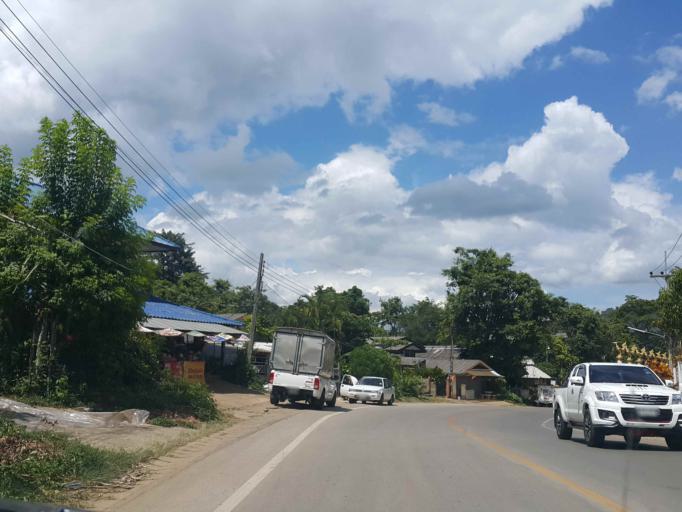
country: TH
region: Chiang Mai
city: Samoeng
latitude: 18.8843
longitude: 98.8189
